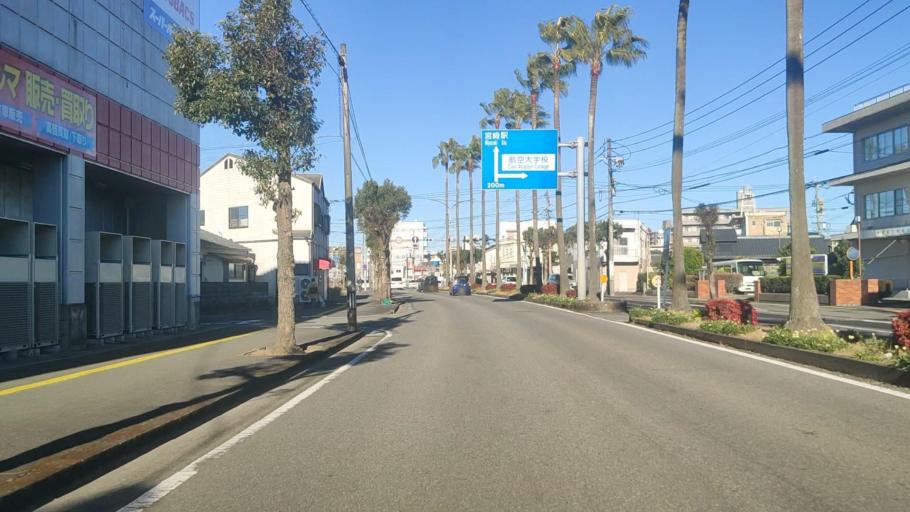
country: JP
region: Miyazaki
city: Miyazaki-shi
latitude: 31.8975
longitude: 131.4236
